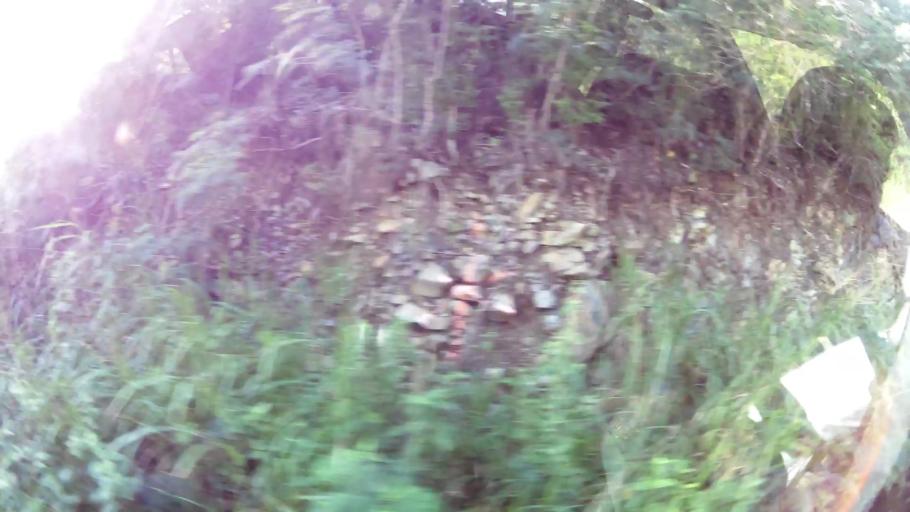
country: VG
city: Tortola
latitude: 18.4337
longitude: -64.5770
